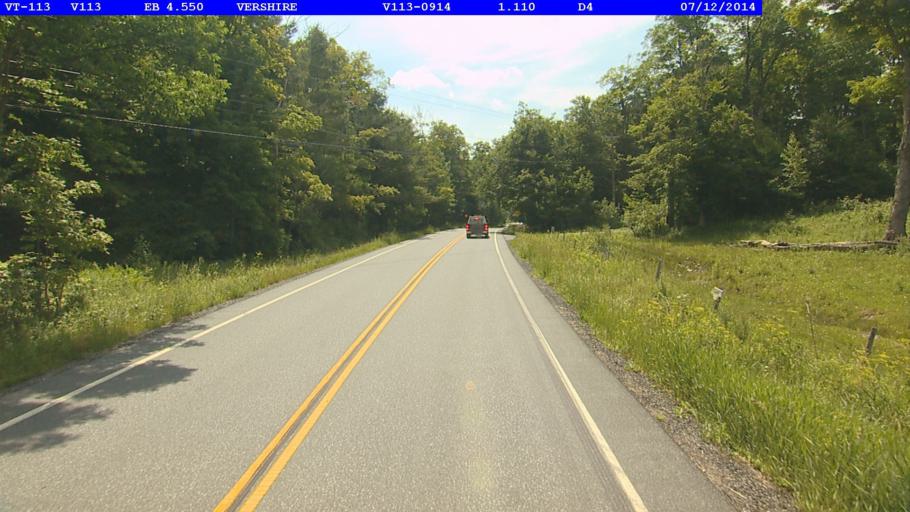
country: US
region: Vermont
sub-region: Orange County
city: Chelsea
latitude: 43.9848
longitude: -72.3652
